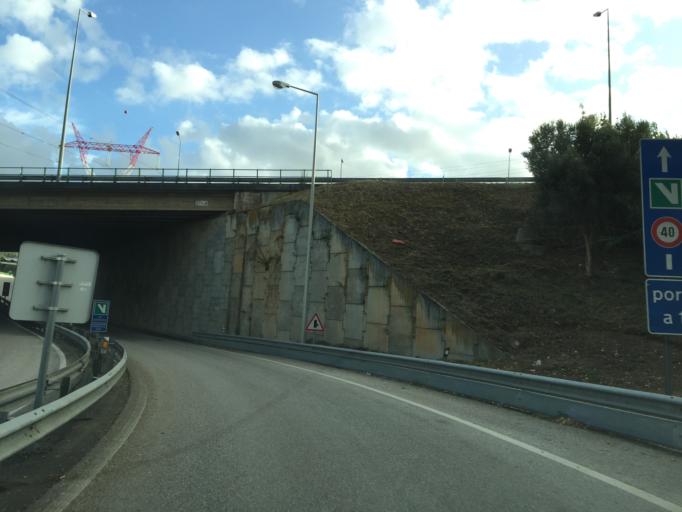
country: PT
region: Coimbra
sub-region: Coimbra
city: Coimbra
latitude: 40.2026
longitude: -8.4905
